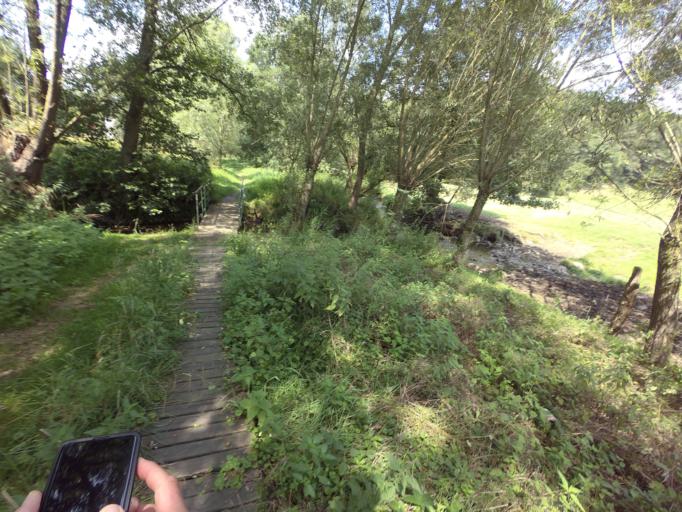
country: BE
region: Wallonia
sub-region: Province de Liege
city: Lontzen
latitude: 50.6925
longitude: 6.0029
